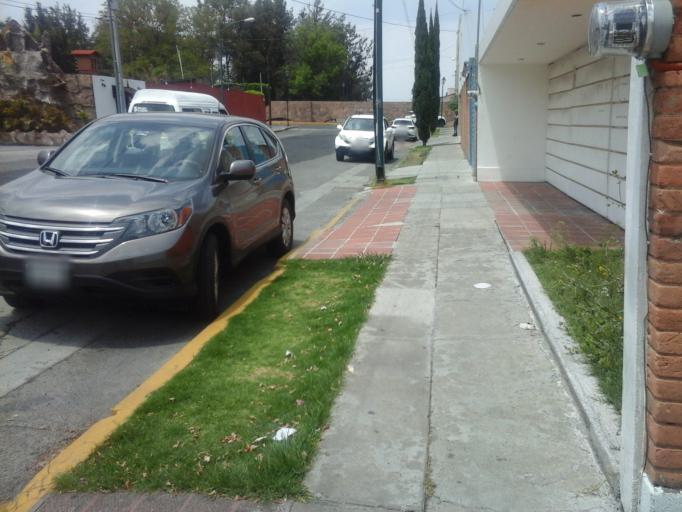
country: MX
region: Michoacan
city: Morelia
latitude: 19.6965
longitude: -101.1708
